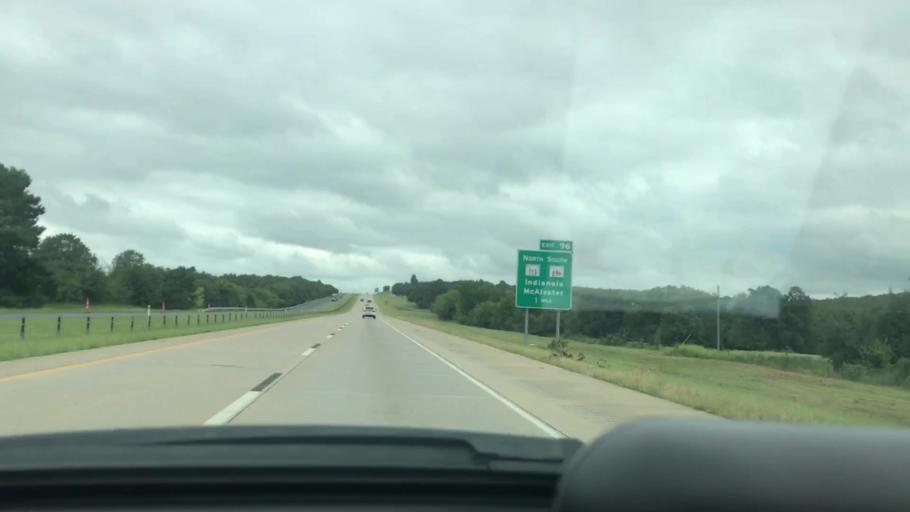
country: US
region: Oklahoma
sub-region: Pittsburg County
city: Krebs
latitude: 34.9788
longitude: -95.7228
